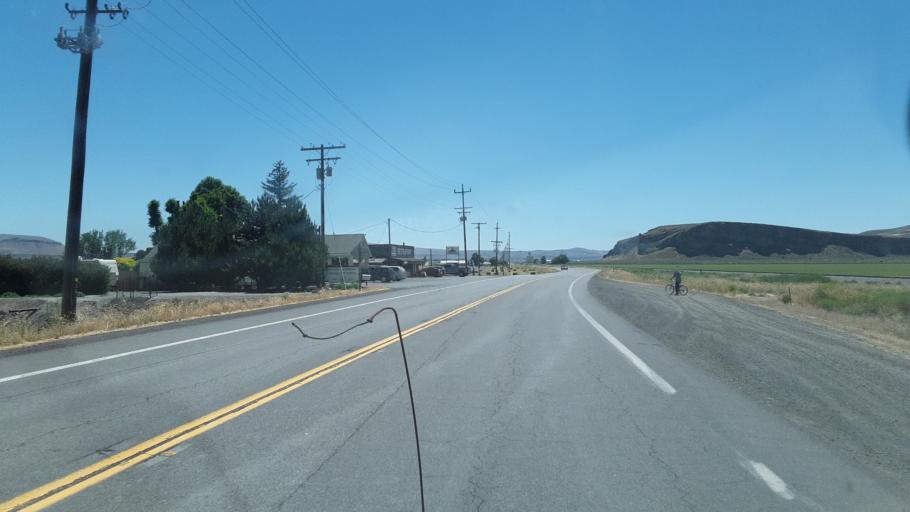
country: US
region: California
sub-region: Siskiyou County
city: Tulelake
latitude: 41.9002
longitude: -121.3986
